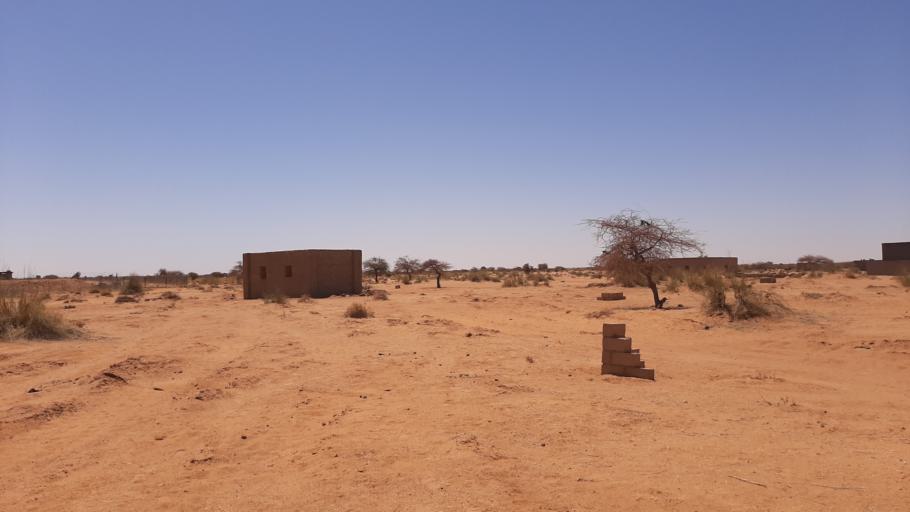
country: ML
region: Gao
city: Gao
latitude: 16.2444
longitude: -0.0250
